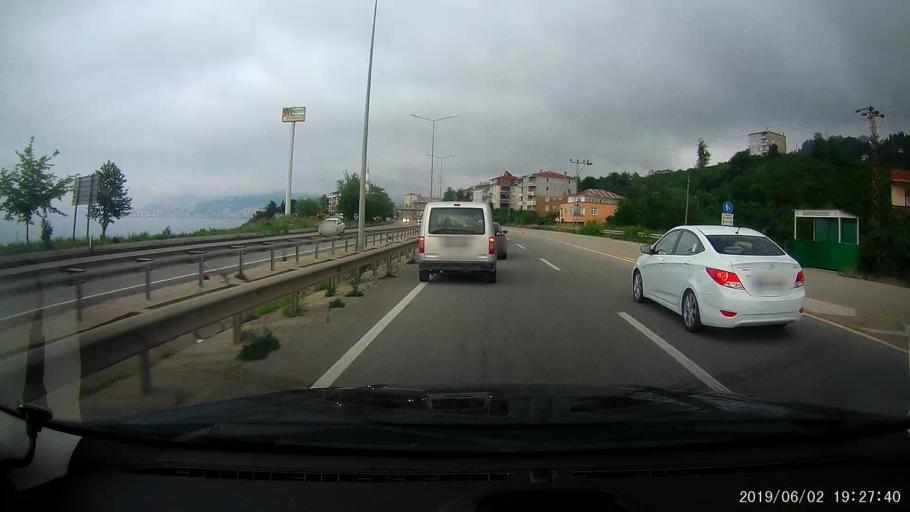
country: TR
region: Giresun
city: Giresun
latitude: 40.9292
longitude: 38.3087
